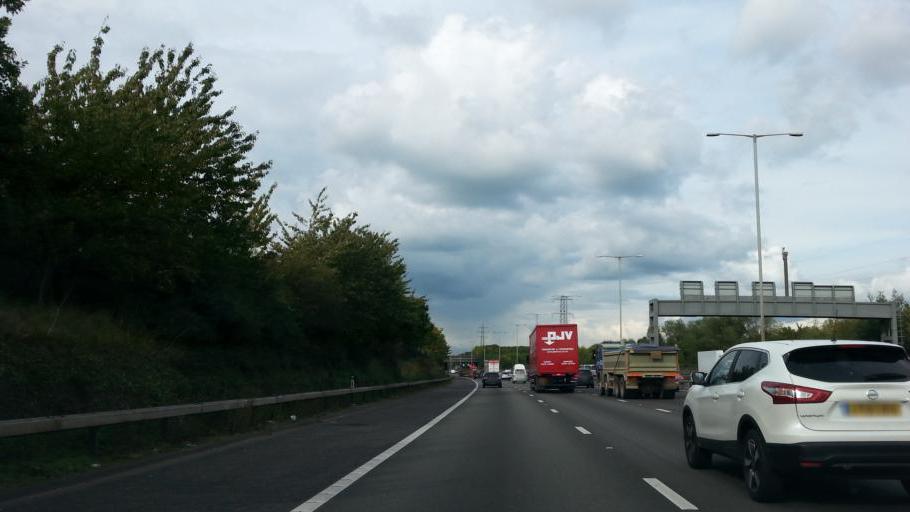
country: GB
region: England
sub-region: Buckinghamshire
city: Iver
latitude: 51.5177
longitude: -0.4996
